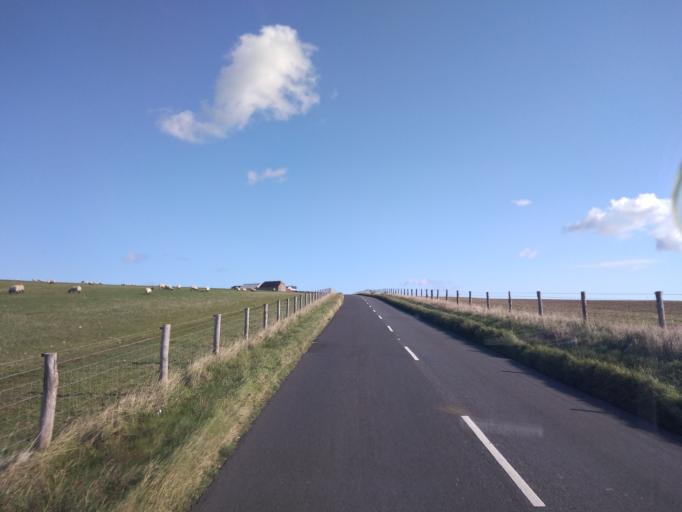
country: GB
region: England
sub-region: East Sussex
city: Seaford
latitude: 50.7861
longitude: 0.1326
